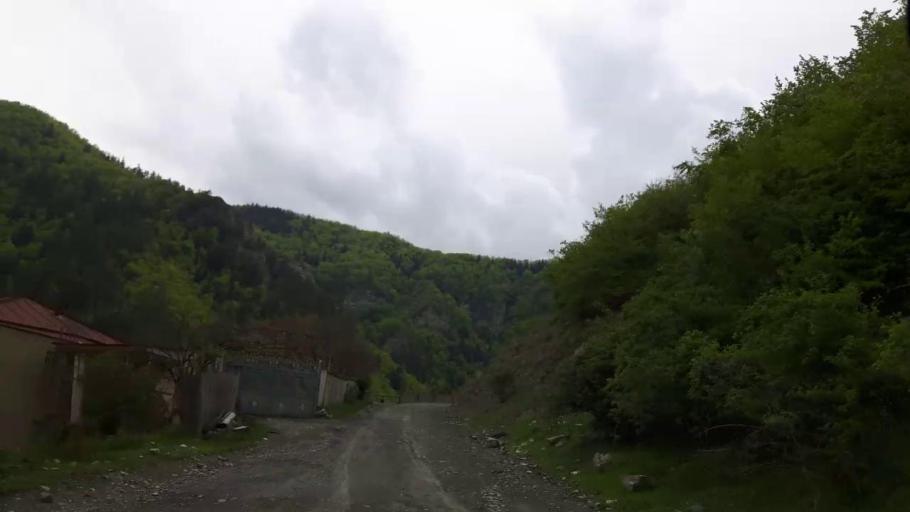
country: GE
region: Shida Kartli
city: Gori
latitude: 41.8666
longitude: 43.9820
